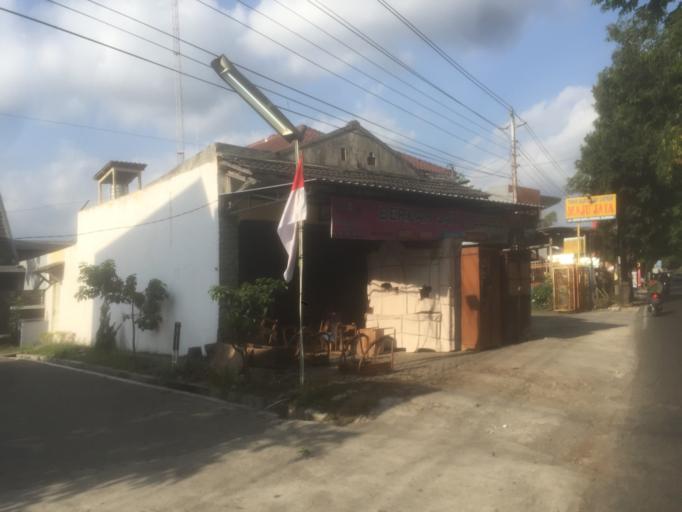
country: ID
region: Daerah Istimewa Yogyakarta
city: Melati
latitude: -7.7189
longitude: 110.3716
